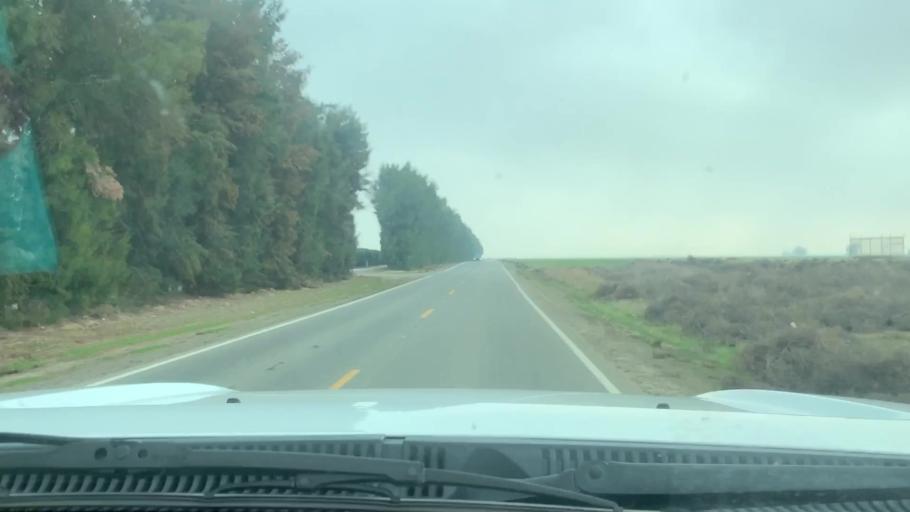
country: US
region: California
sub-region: Kern County
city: Lost Hills
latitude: 35.5211
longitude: -119.7557
